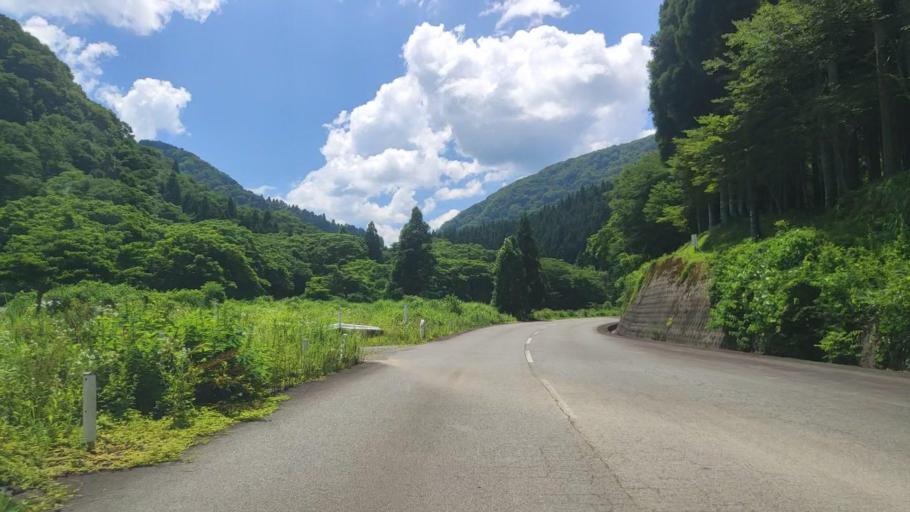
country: JP
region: Fukui
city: Ono
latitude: 35.8559
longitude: 136.4663
